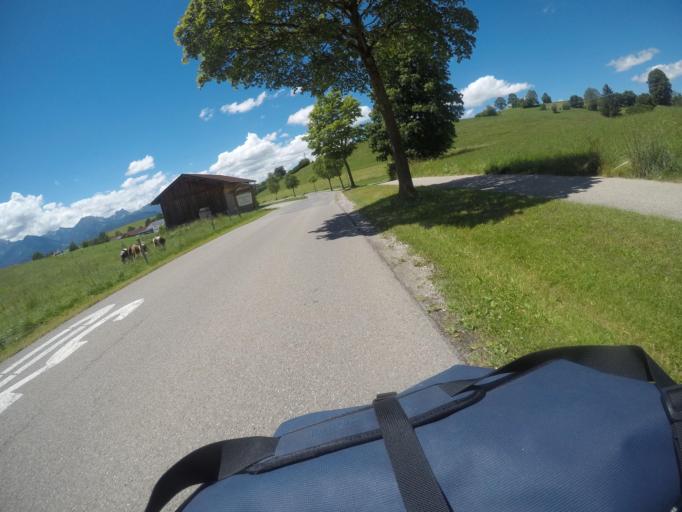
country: DE
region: Bavaria
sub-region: Swabia
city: Rosshaupten
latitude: 47.6143
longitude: 10.7193
